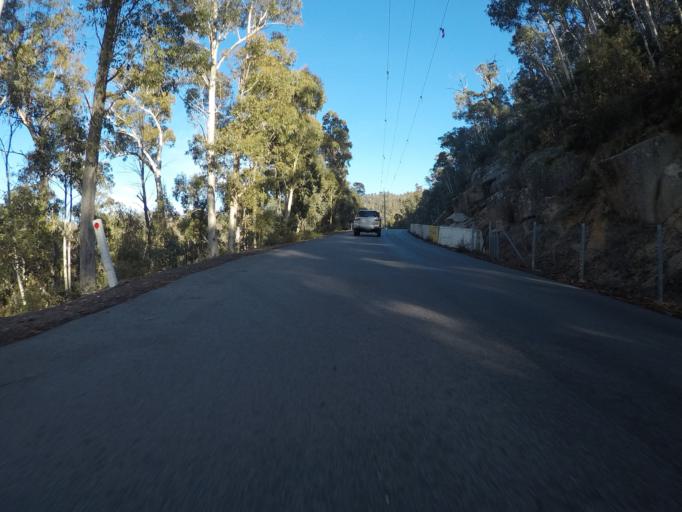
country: AU
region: Australian Capital Territory
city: Macarthur
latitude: -35.4919
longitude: 148.9308
